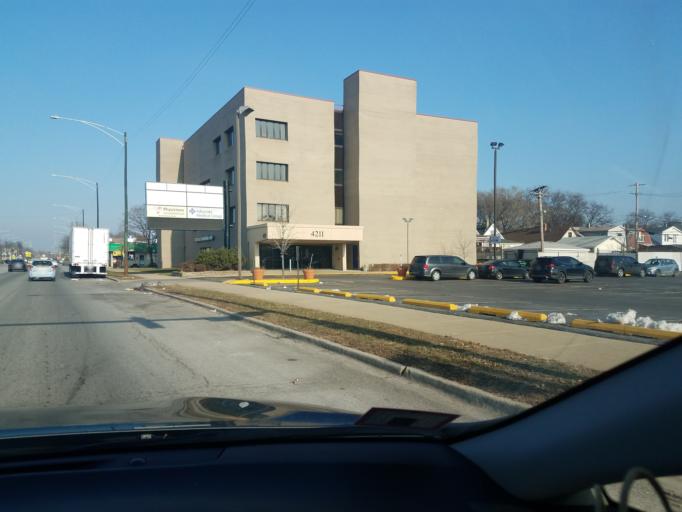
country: US
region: Illinois
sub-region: Cook County
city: Lincolnwood
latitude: 41.9571
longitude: -87.7473
